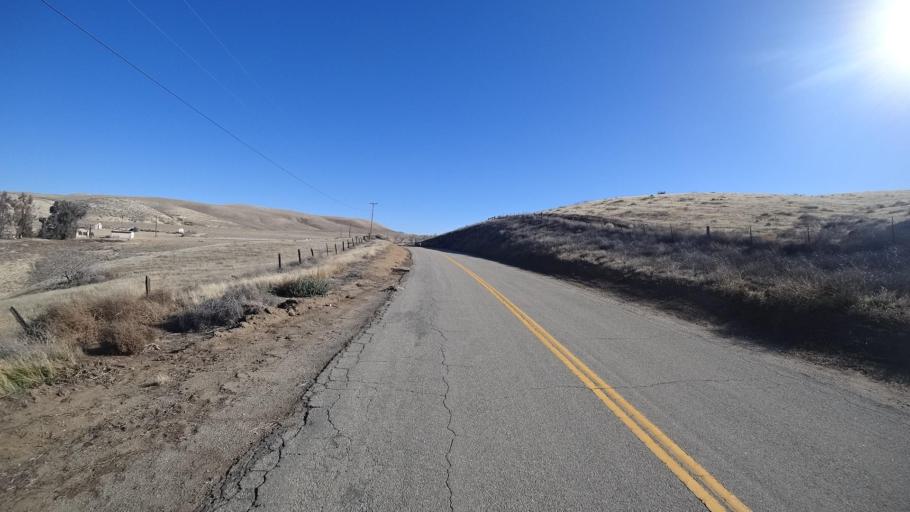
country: US
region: California
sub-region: Kern County
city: Maricopa
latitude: 34.9596
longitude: -119.4450
